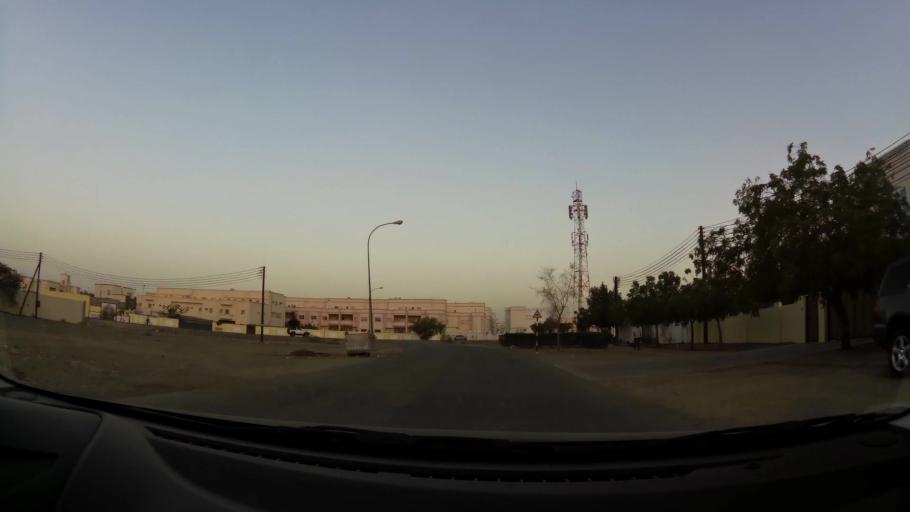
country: OM
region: Muhafazat Masqat
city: As Sib al Jadidah
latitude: 23.6447
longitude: 58.2144
